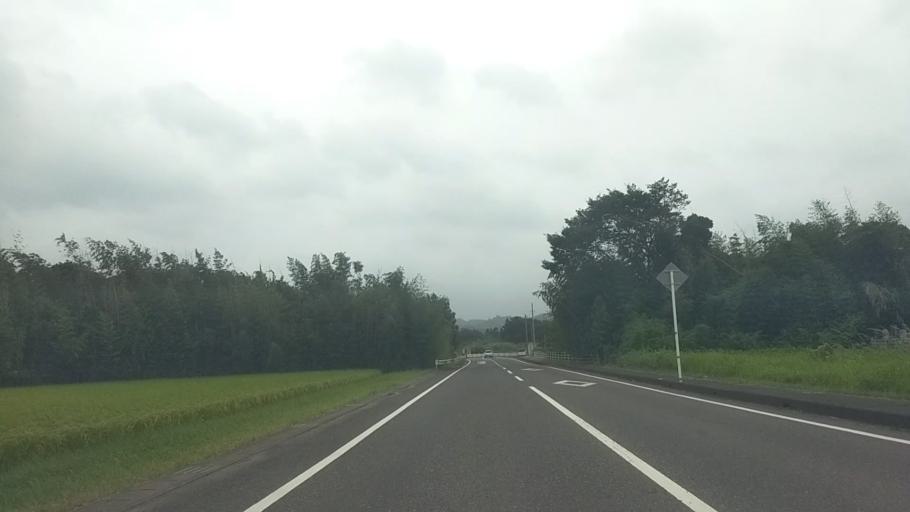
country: JP
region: Chiba
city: Kimitsu
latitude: 35.2189
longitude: 139.9168
